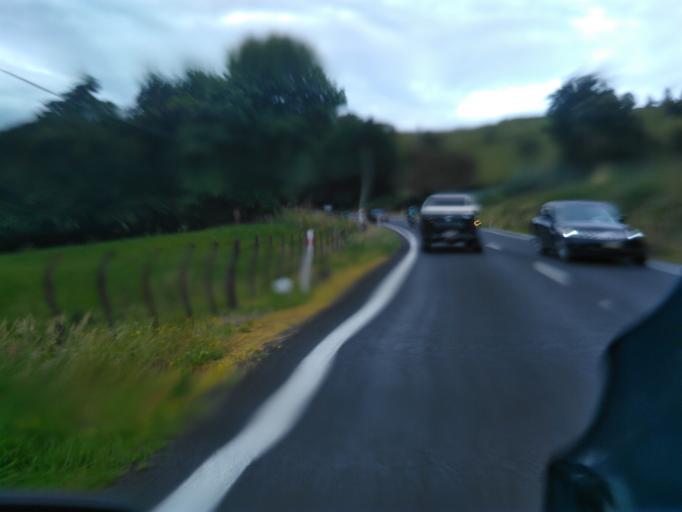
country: NZ
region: Gisborne
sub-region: Gisborne District
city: Gisborne
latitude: -38.4762
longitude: 177.6803
